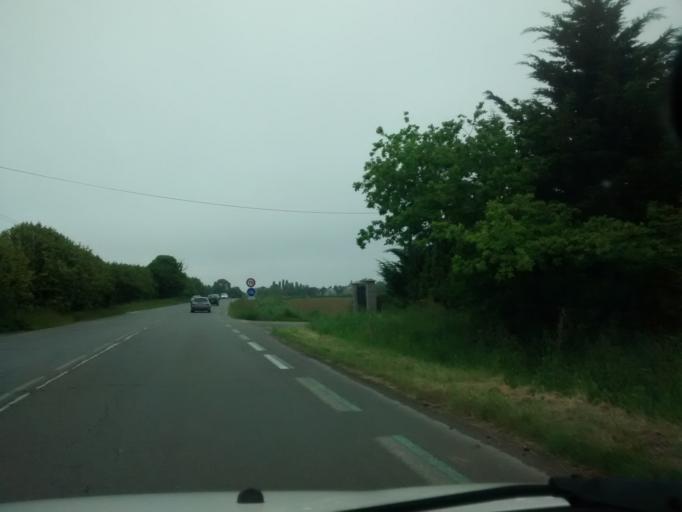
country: FR
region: Brittany
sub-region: Departement d'Ille-et-Vilaine
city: Saint-Gregoire
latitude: 48.1434
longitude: -1.7022
